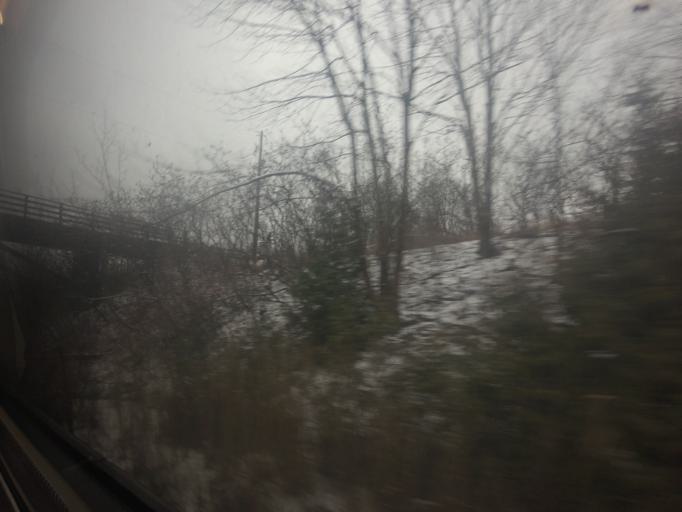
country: CA
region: Ontario
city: Cobourg
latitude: 43.9244
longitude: -78.4270
